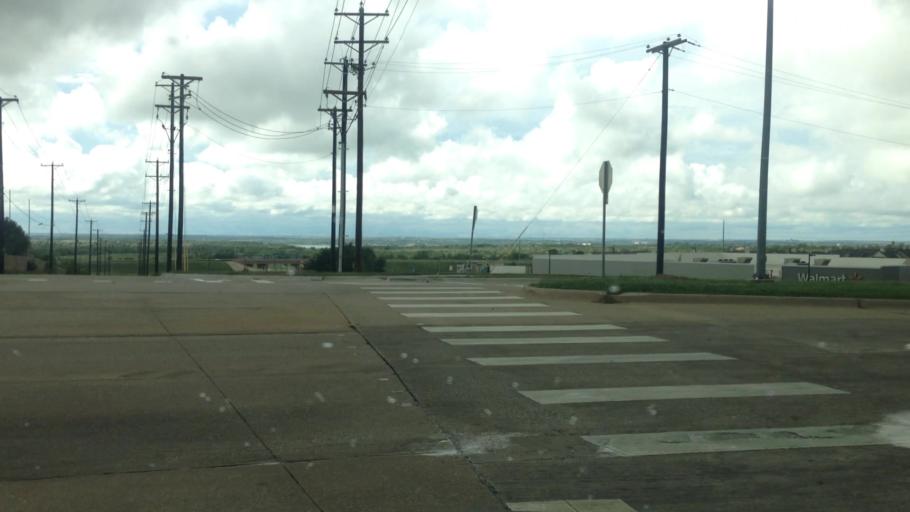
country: US
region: Texas
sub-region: Tarrant County
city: Crowley
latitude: 32.6289
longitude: -97.4063
